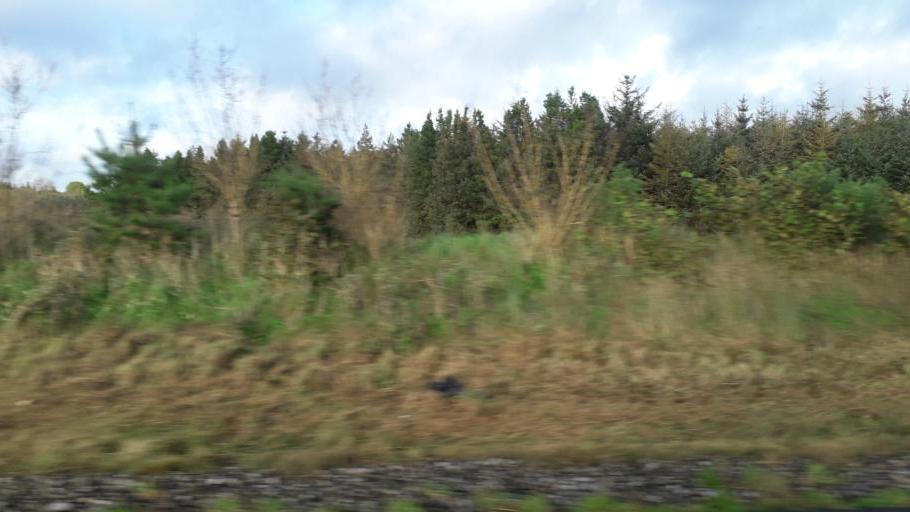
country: IE
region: Connaught
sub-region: Roscommon
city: Ballaghaderreen
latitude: 53.8913
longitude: -8.5031
